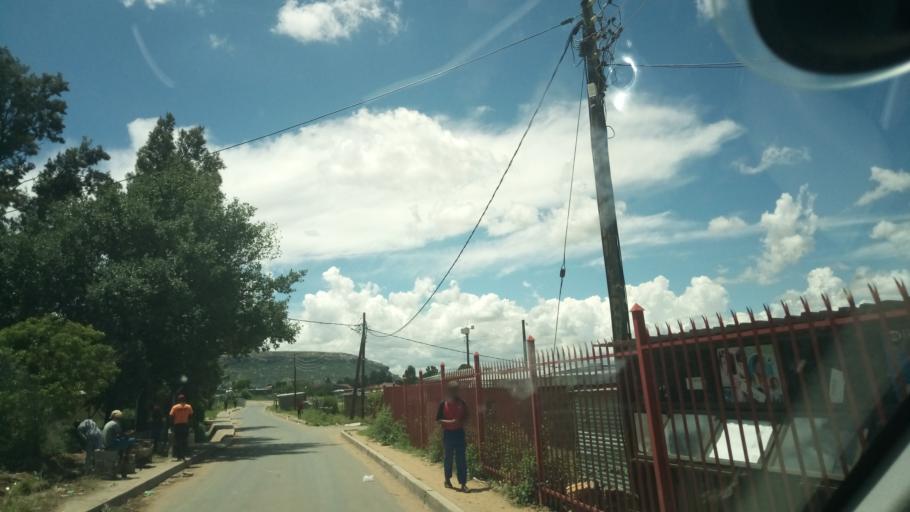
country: LS
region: Maseru
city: Maseru
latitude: -29.3686
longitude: 27.5386
